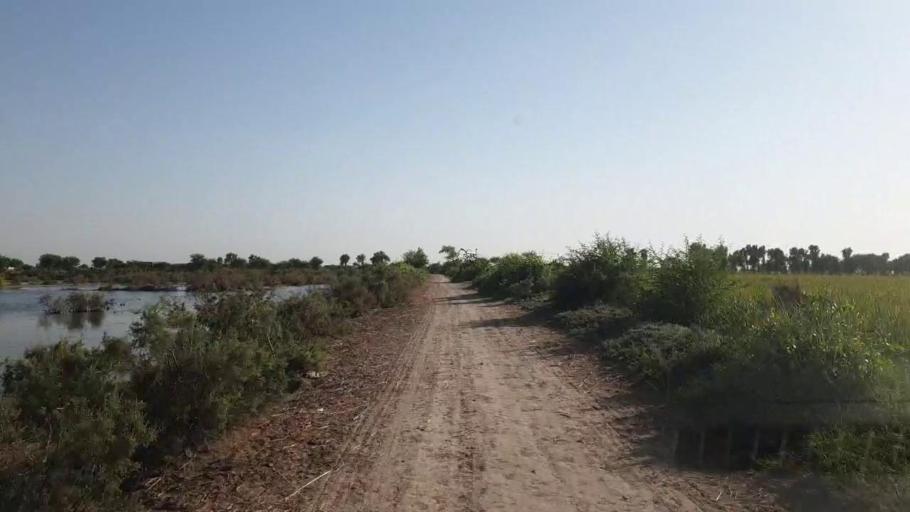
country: PK
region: Sindh
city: Badin
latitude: 24.5942
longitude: 68.9110
